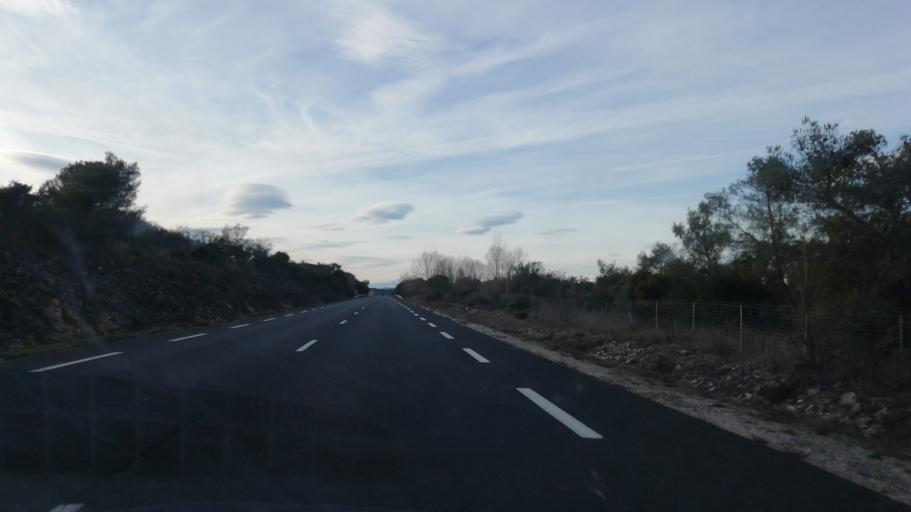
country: FR
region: Languedoc-Roussillon
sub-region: Departement du Gard
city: Clarensac
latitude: 43.8578
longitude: 4.2345
